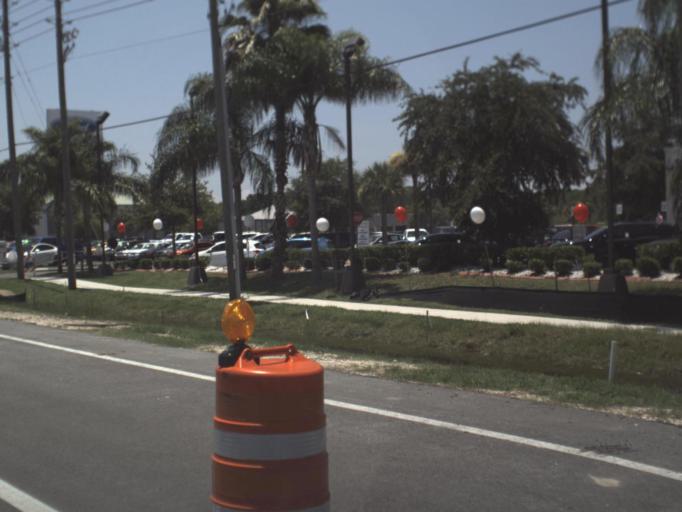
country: US
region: Florida
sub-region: Pasco County
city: Bayonet Point
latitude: 28.3143
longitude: -82.6994
